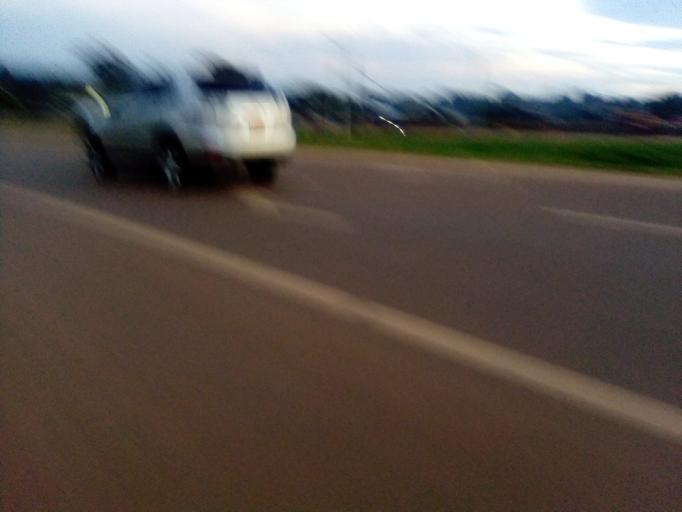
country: UG
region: Central Region
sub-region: Wakiso District
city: Entebbe
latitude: 0.1053
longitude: 32.5130
